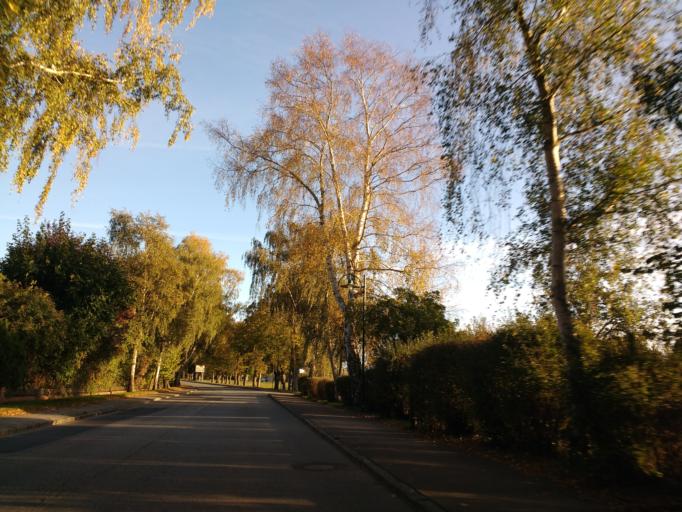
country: DE
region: Schleswig-Holstein
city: Kellenhusen
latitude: 54.1943
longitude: 11.0528
